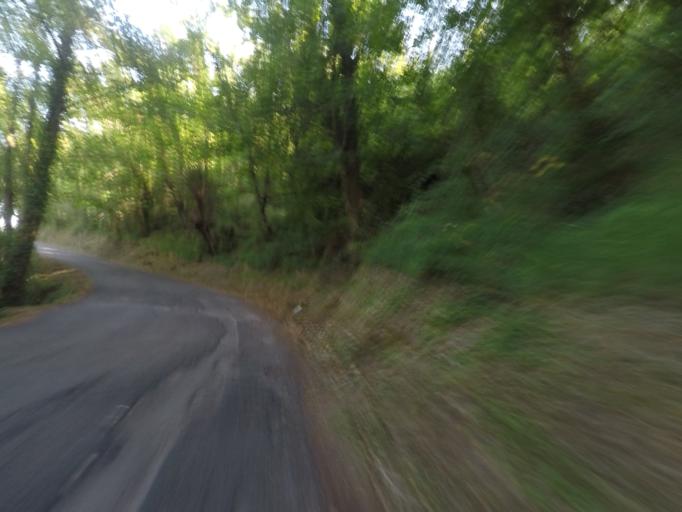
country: IT
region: Tuscany
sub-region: Provincia di Massa-Carrara
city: Carrara
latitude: 44.0731
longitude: 10.0685
